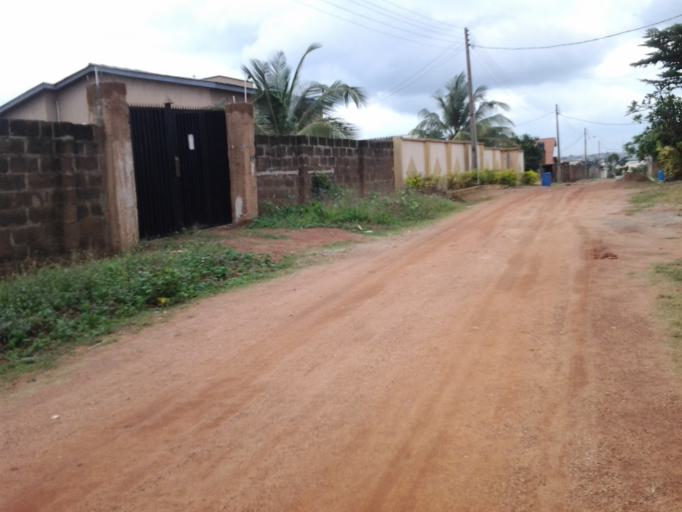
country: NG
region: Oyo
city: Ibadan
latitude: 7.4370
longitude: 3.9564
